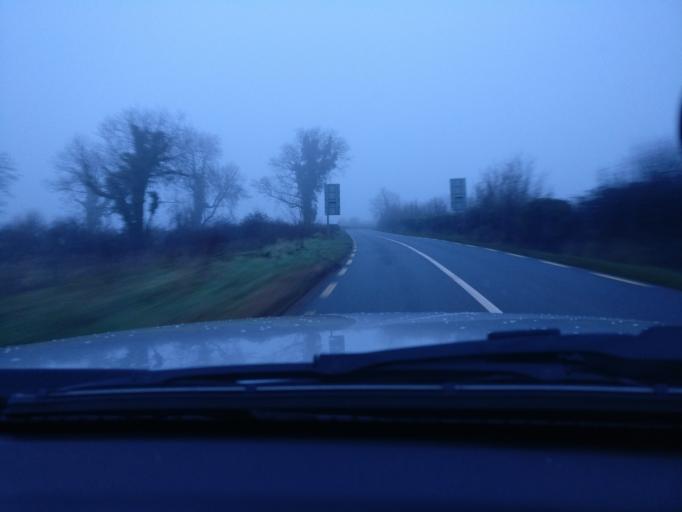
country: IE
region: Leinster
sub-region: An Mhi
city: Athboy
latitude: 53.6300
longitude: -6.9014
